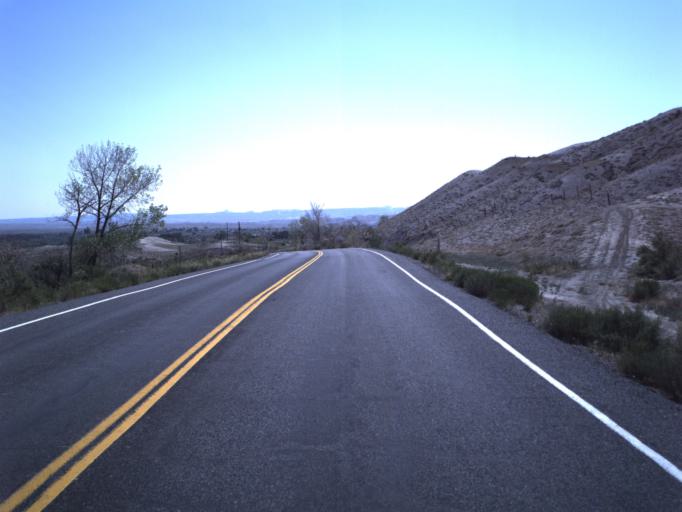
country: US
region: Utah
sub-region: Emery County
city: Orangeville
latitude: 39.2139
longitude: -111.0588
